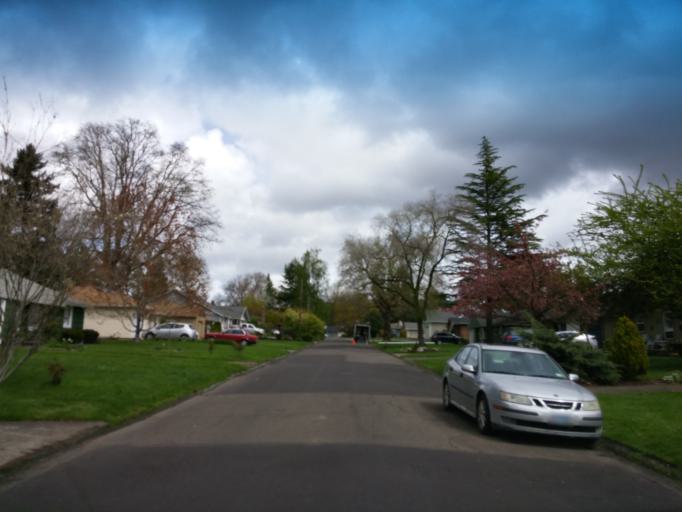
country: US
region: Oregon
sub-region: Washington County
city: Cedar Hills
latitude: 45.5058
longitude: -122.8012
